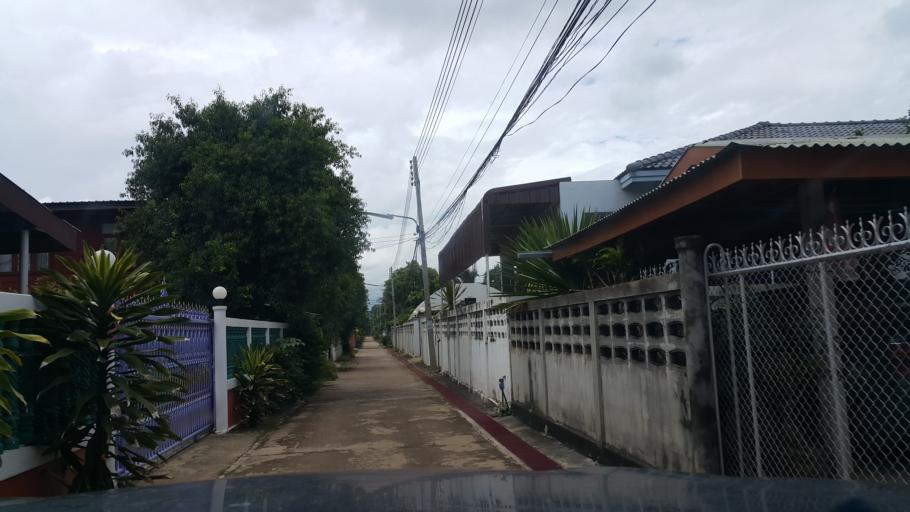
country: TH
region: Sukhothai
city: Thung Saliam
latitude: 17.3190
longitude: 99.5495
